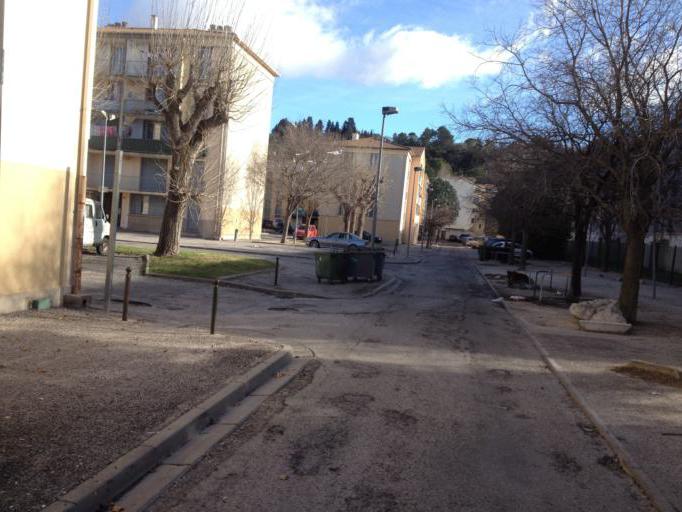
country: FR
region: Provence-Alpes-Cote d'Azur
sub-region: Departement du Vaucluse
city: Orange
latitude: 44.1303
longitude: 4.8005
